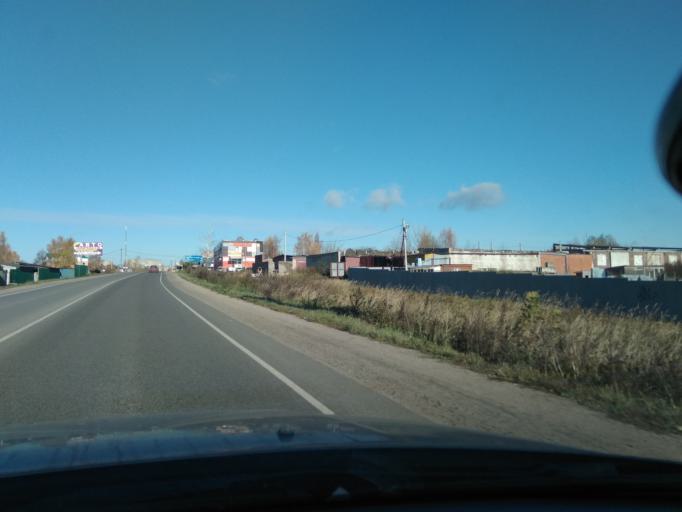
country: RU
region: Moskovskaya
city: Istra
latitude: 55.8956
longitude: 36.8621
